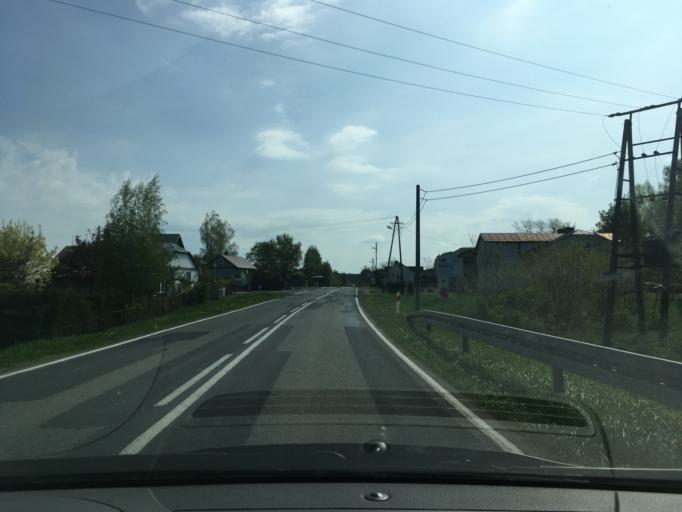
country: PL
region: Lublin Voivodeship
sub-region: Powiat pulawski
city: Pulawy
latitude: 51.4752
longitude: 21.9045
